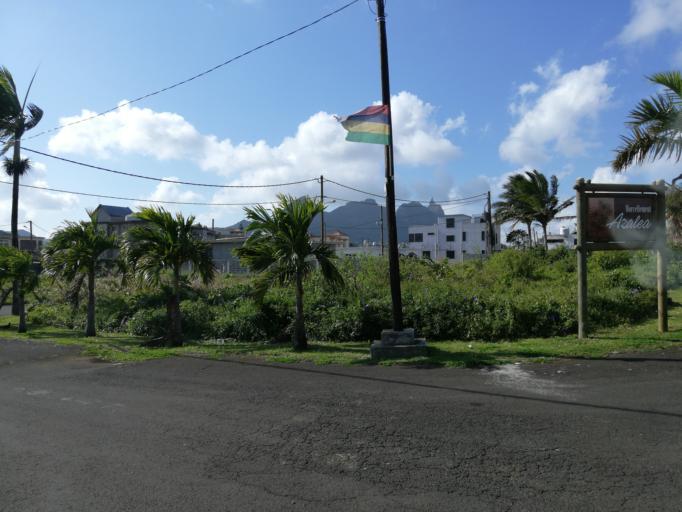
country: MU
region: Moka
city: Verdun
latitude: -20.2222
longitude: 57.5471
